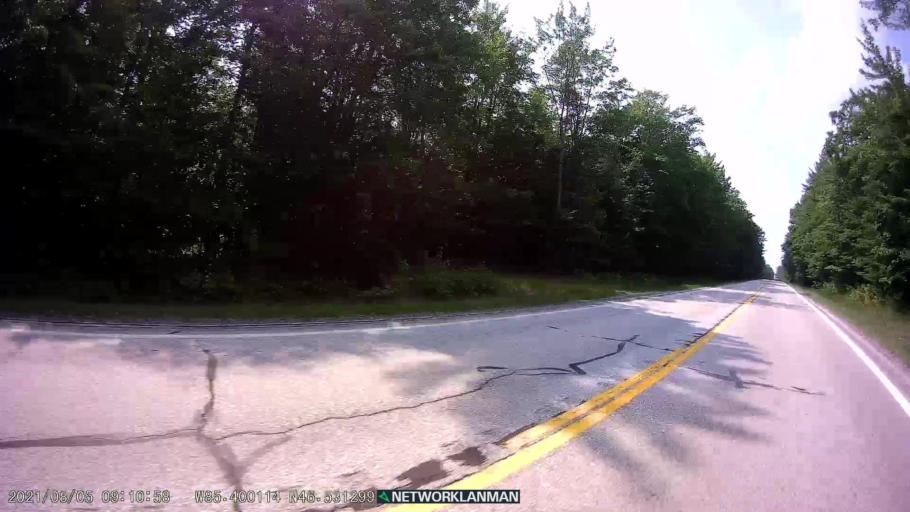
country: US
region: Michigan
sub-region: Luce County
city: Newberry
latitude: 46.5310
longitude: -85.4005
